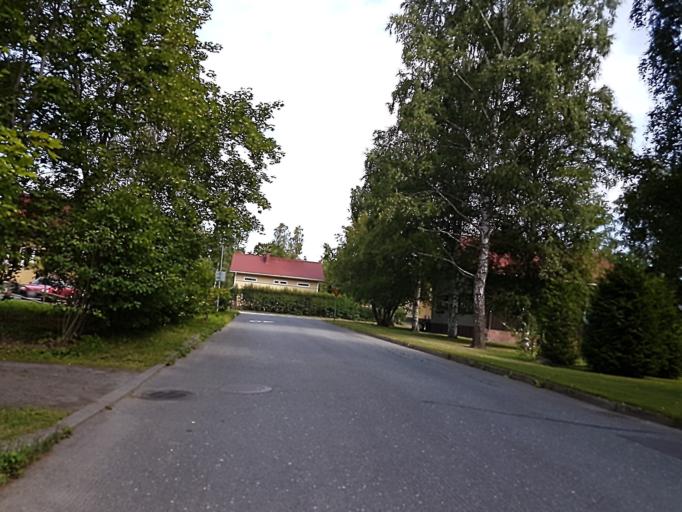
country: FI
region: Pirkanmaa
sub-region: Etelae-Pirkanmaa
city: Valkeakoski
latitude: 61.2508
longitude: 24.0498
